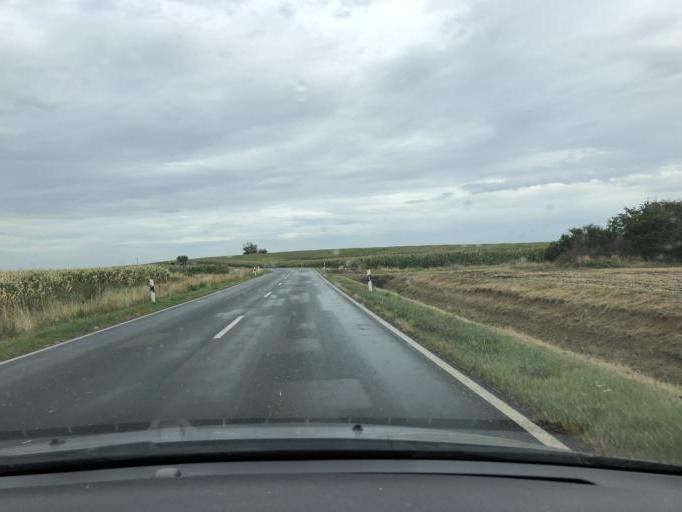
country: DE
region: Saxony-Anhalt
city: Gross Rosenburg
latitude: 51.8575
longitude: 11.8588
